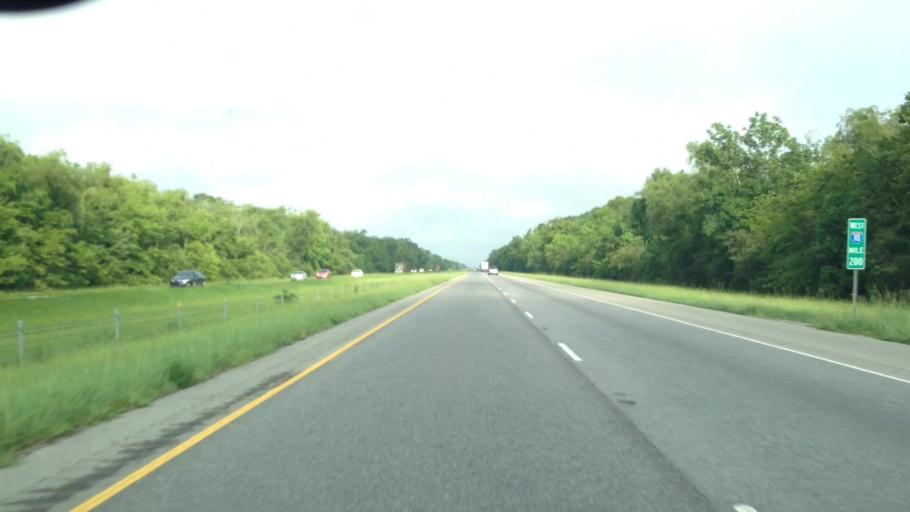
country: US
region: Louisiana
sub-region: Saint John the Baptist Parish
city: Garyville
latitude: 30.1159
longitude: -90.5976
